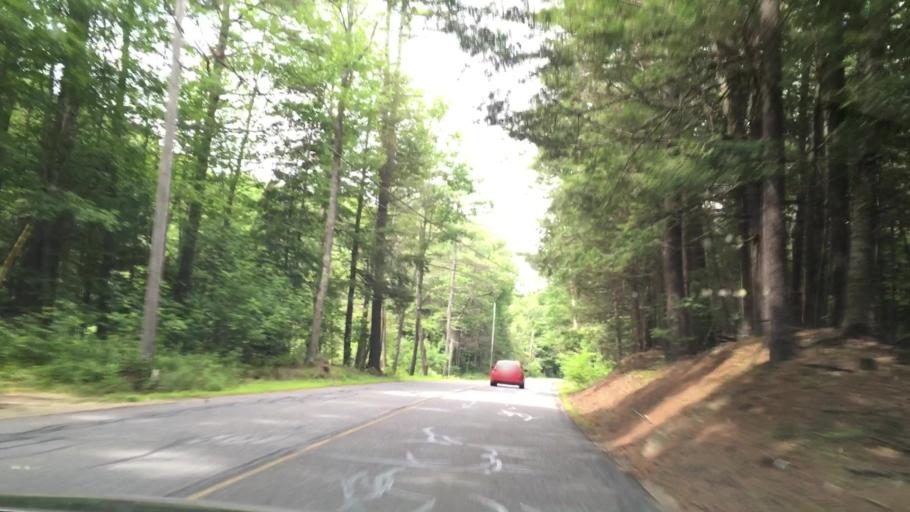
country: US
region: Massachusetts
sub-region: Worcester County
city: Winchendon
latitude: 42.6992
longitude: -72.0148
